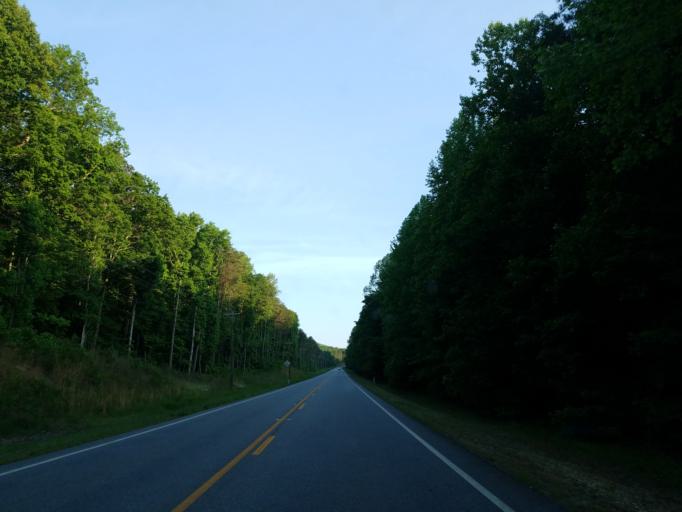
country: US
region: Georgia
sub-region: Whitfield County
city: Dalton
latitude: 34.6732
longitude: -85.0625
